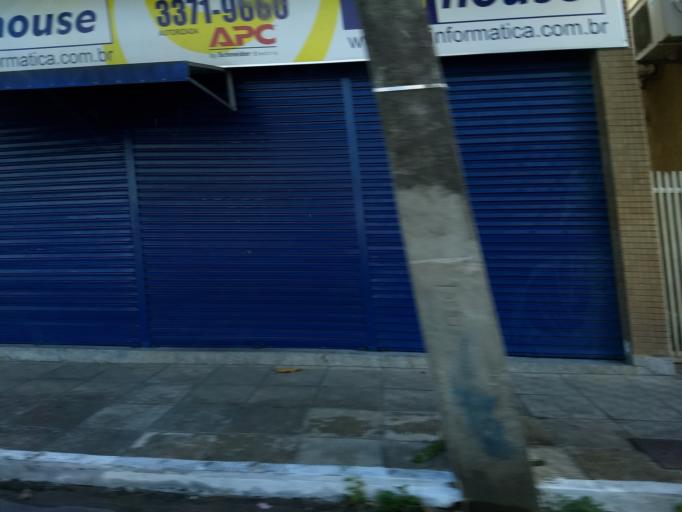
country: BR
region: Santa Catarina
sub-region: Jaragua Do Sul
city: Jaragua do Sul
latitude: -26.4776
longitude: -49.0815
